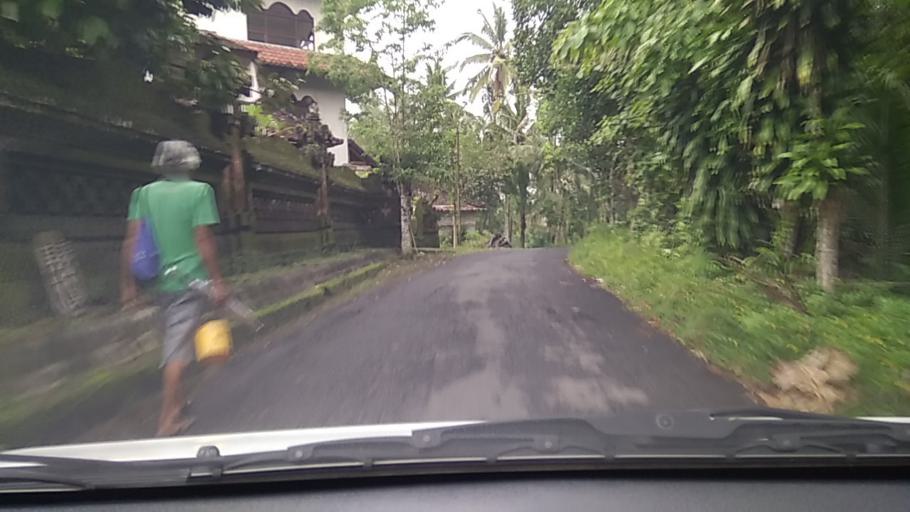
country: ID
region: Bali
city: Banjar Dujung Kaja
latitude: -8.4129
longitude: 115.2852
